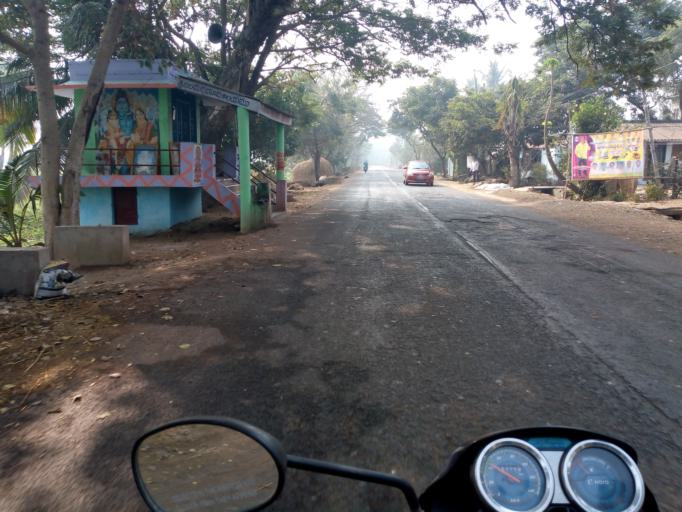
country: IN
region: Andhra Pradesh
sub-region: West Godavari
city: Tadepallegudem
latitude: 16.7834
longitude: 81.4198
